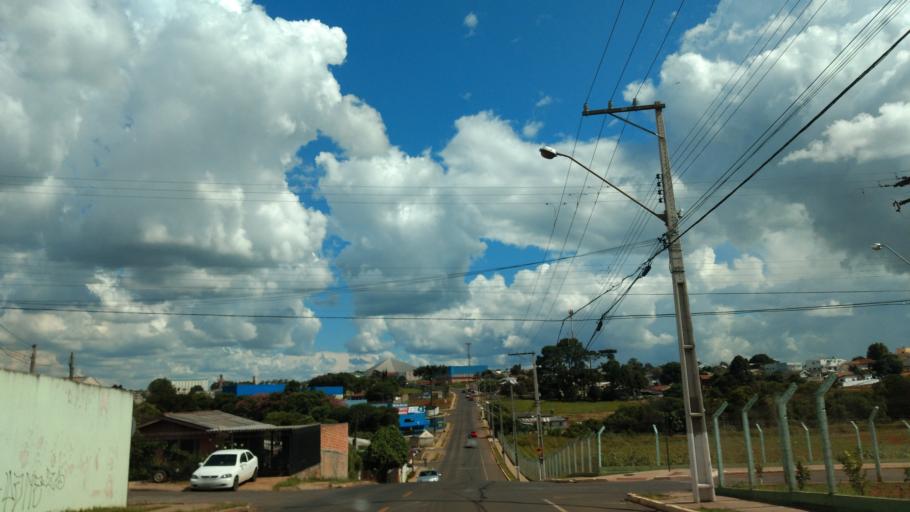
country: BR
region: Parana
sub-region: Guarapuava
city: Guarapuava
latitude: -25.3947
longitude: -51.4929
